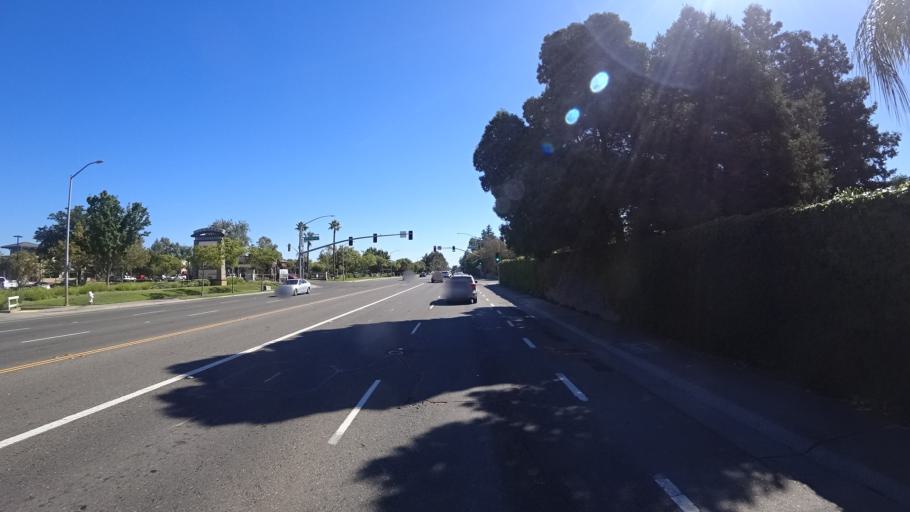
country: US
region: California
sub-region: Sacramento County
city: Elk Grove
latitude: 38.4234
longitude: -121.3885
